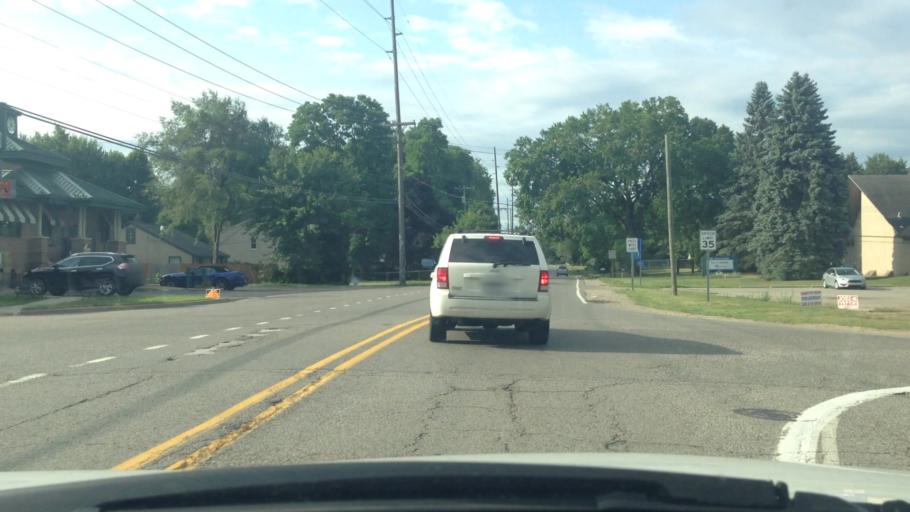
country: US
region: Michigan
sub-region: Oakland County
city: Waterford
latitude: 42.7055
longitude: -83.3487
